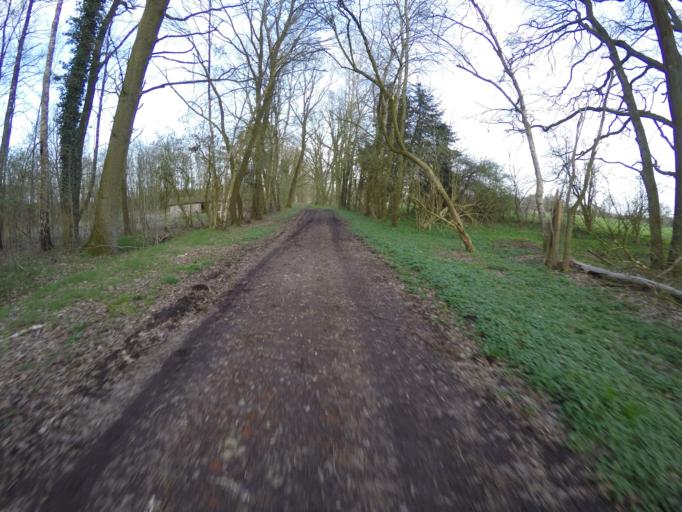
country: DE
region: Schleswig-Holstein
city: Hemdingen
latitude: 53.7279
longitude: 9.8507
